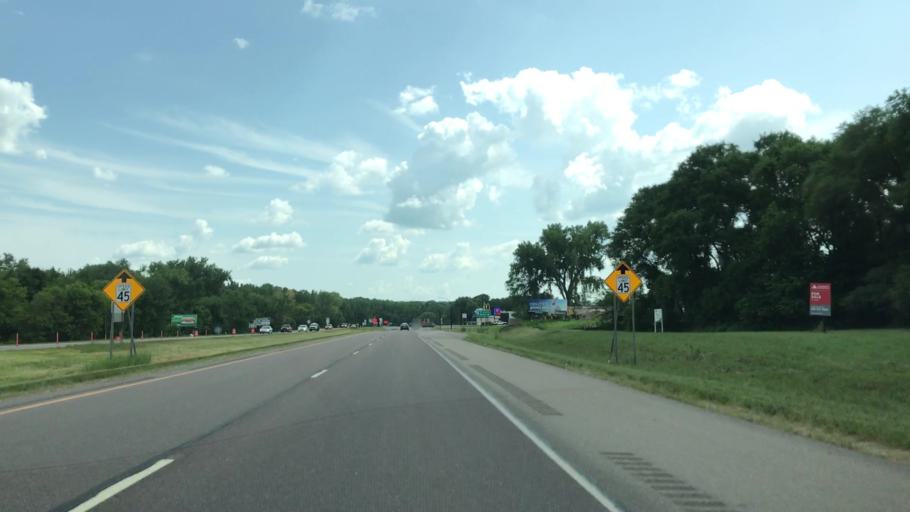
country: US
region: Minnesota
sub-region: Nicollet County
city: Saint Peter
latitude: 44.3428
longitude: -93.9496
